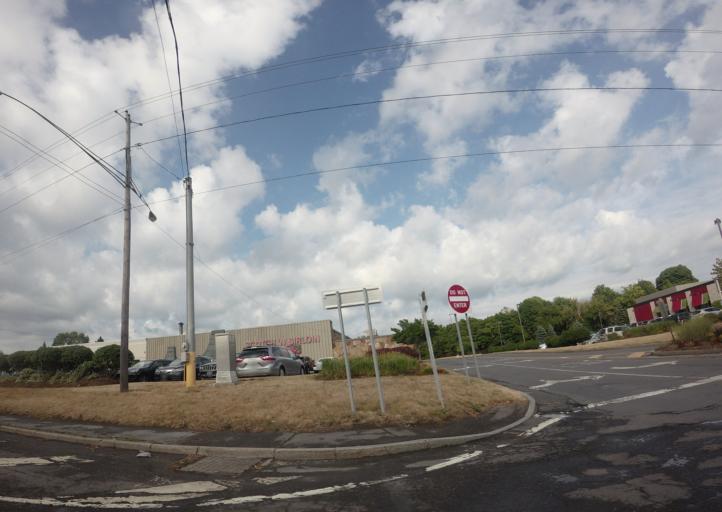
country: US
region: New York
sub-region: Onondaga County
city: East Syracuse
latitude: 43.0374
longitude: -76.0654
